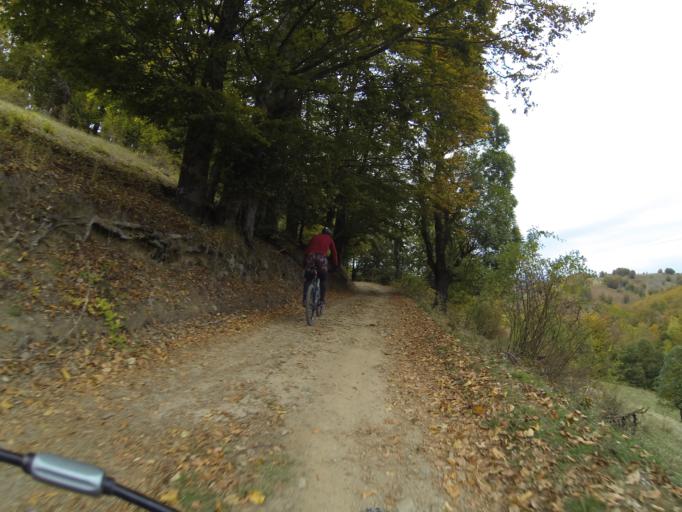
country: RO
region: Gorj
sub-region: Comuna Pades
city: Closani
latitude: 45.1008
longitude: 22.8410
